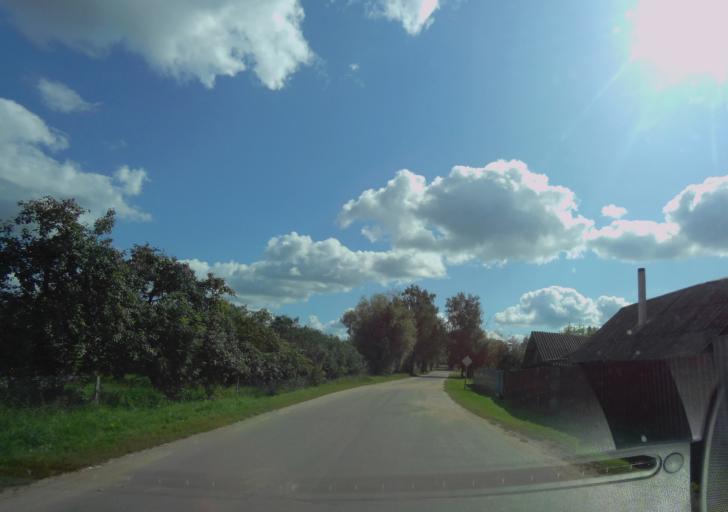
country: BY
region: Minsk
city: Horad Barysaw
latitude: 54.4297
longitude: 28.4316
